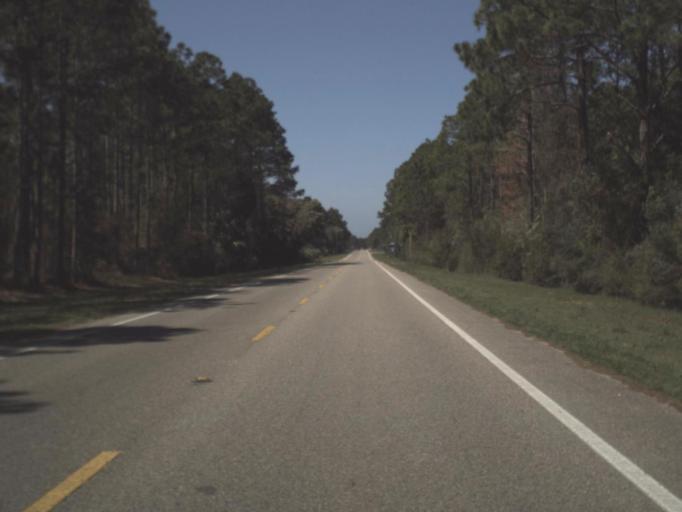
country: US
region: Florida
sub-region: Gulf County
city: Port Saint Joe
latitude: 29.7765
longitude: -85.2743
